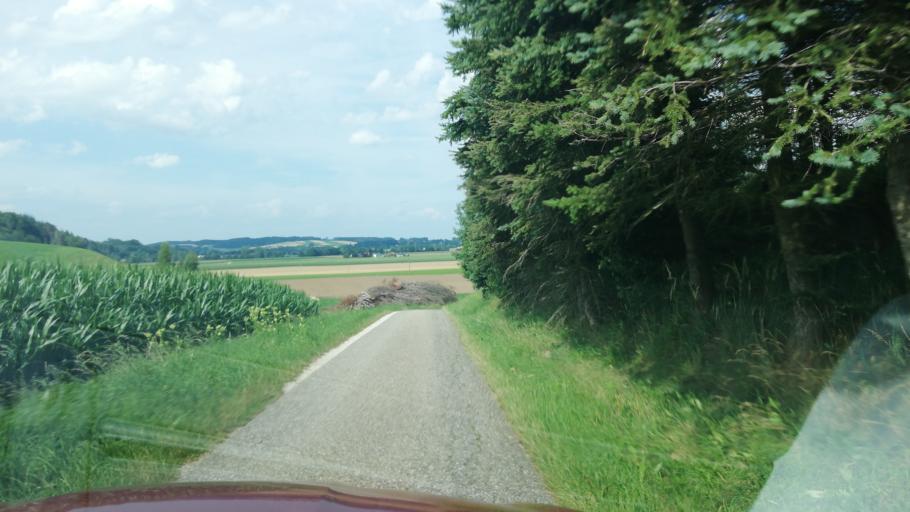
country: AT
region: Upper Austria
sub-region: Politischer Bezirk Vocklabruck
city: Redlham
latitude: 48.0378
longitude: 13.7409
